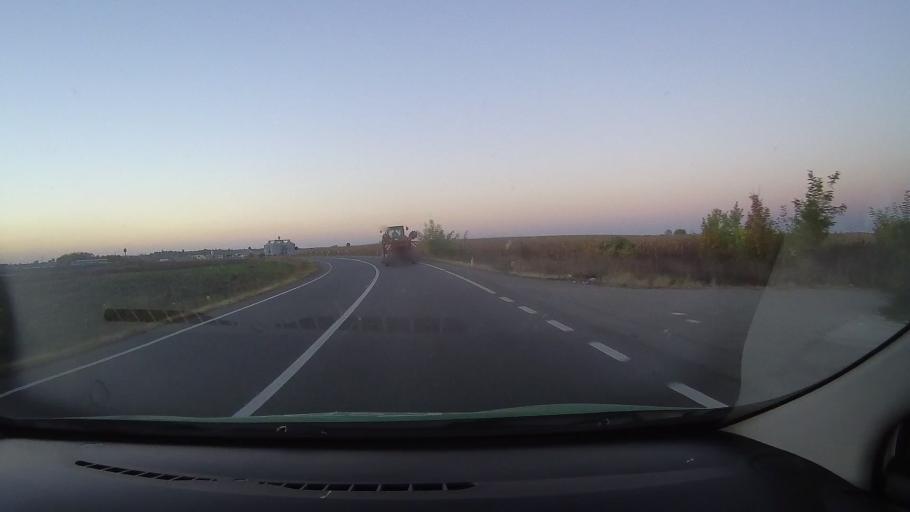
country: RO
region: Bihor
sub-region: Comuna Tarcea
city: Tarcea
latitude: 47.4489
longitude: 22.1854
